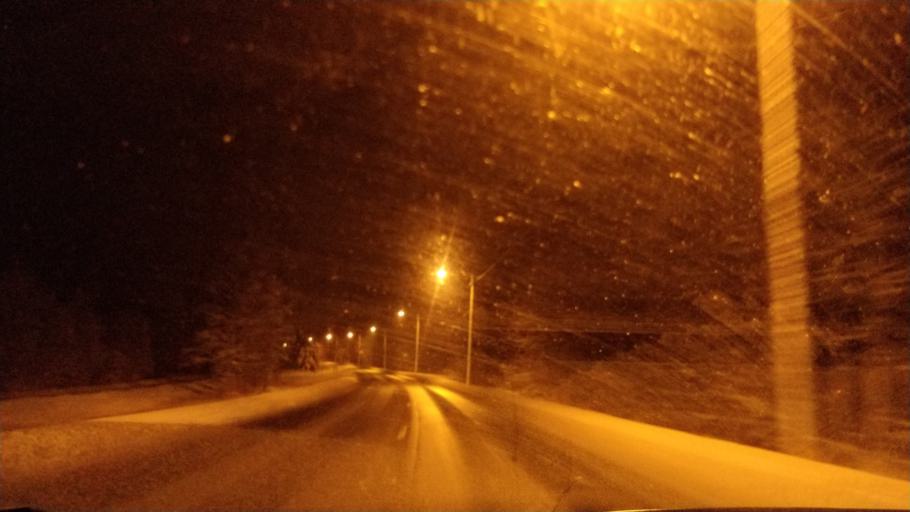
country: FI
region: Lapland
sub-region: Rovaniemi
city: Rovaniemi
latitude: 66.4037
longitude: 25.3913
